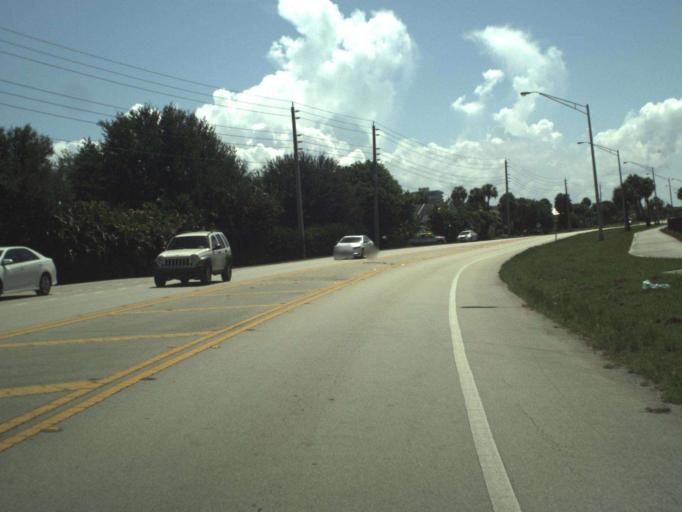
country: US
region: Florida
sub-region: Saint Lucie County
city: Fort Pierce
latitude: 27.4853
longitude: -80.3064
